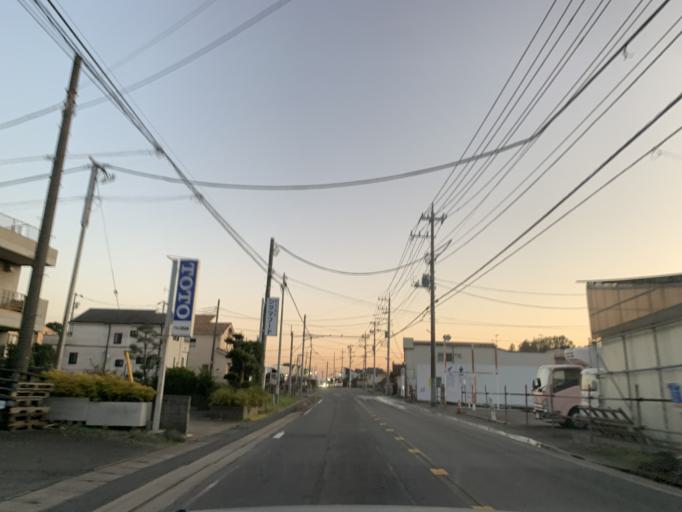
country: JP
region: Chiba
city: Nagareyama
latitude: 35.9036
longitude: 139.9018
